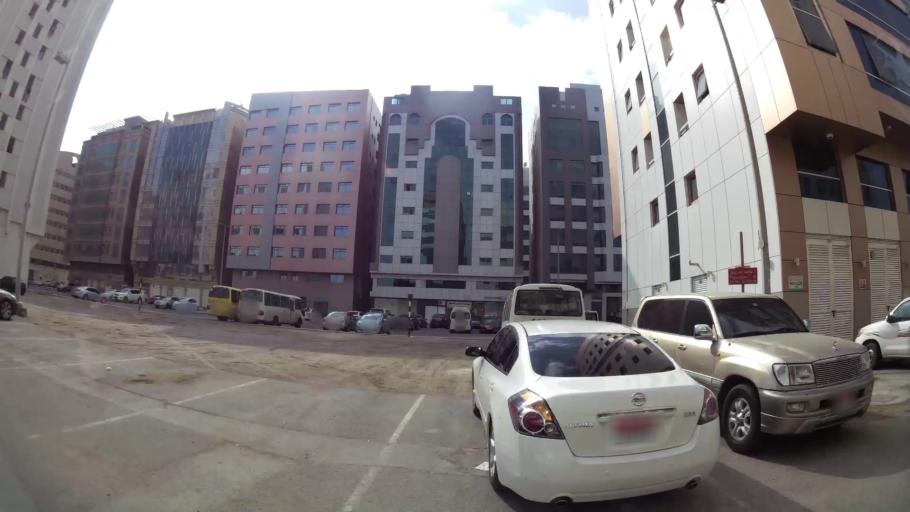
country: AE
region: Abu Dhabi
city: Abu Dhabi
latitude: 24.3196
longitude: 54.5384
